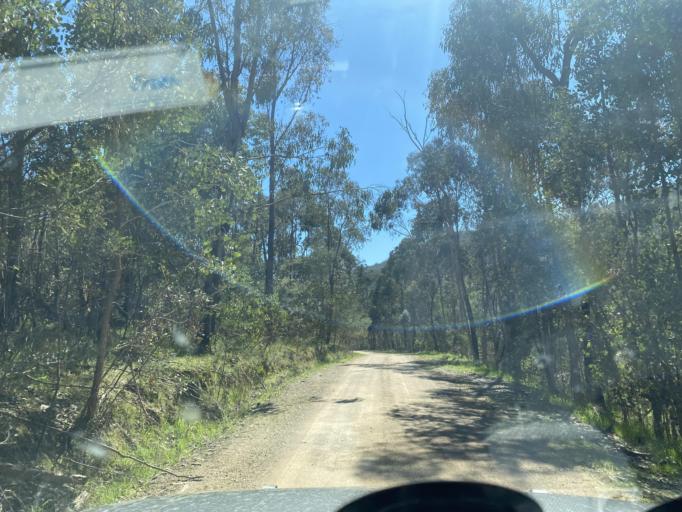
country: AU
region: Victoria
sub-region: Benalla
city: Benalla
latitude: -36.7032
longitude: 146.1784
